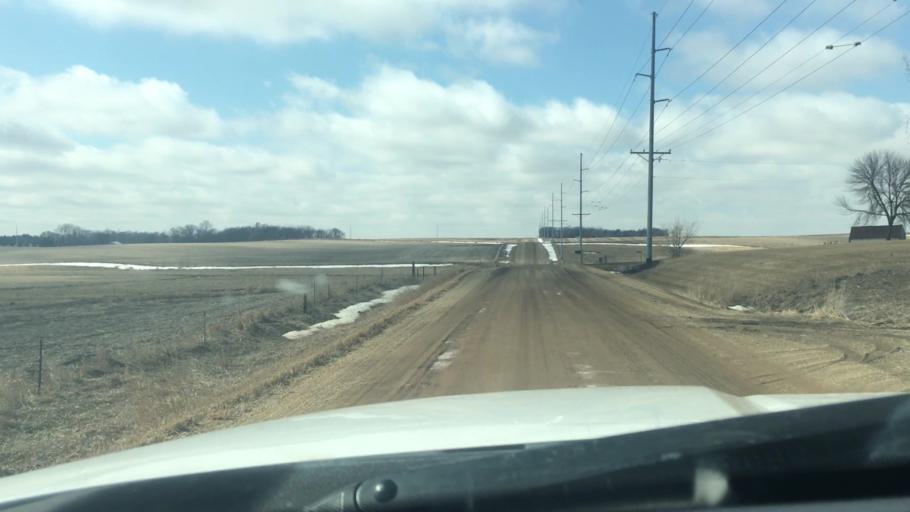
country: US
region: South Dakota
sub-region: Minnehaha County
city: Crooks
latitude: 43.6164
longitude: -96.7986
